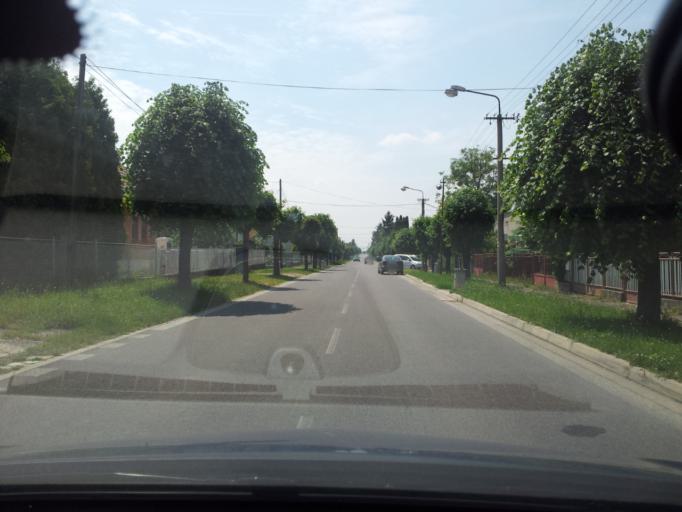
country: SK
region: Nitriansky
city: Zlate Moravce
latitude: 48.3871
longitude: 18.4071
